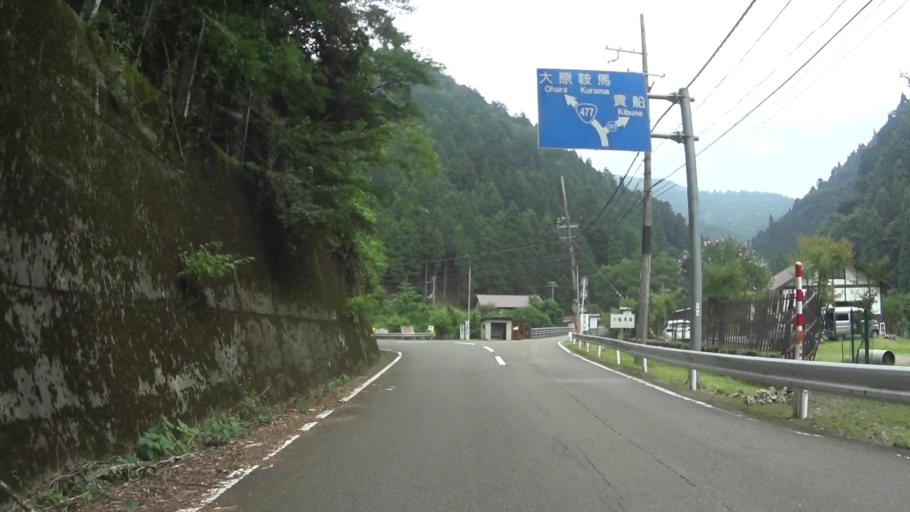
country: JP
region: Shiga Prefecture
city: Kitahama
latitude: 35.2047
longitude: 135.7471
